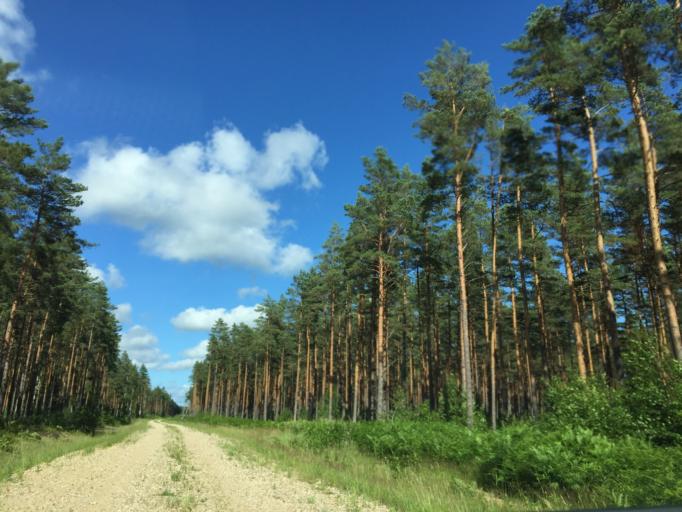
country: LV
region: Ventspils
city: Ventspils
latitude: 57.5314
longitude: 21.7192
